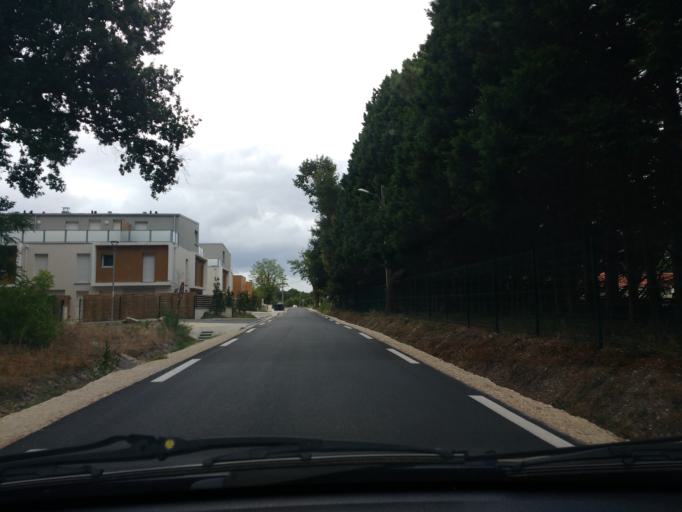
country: FR
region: Aquitaine
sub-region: Departement de la Gironde
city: Canejan
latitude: 44.7799
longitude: -0.6303
